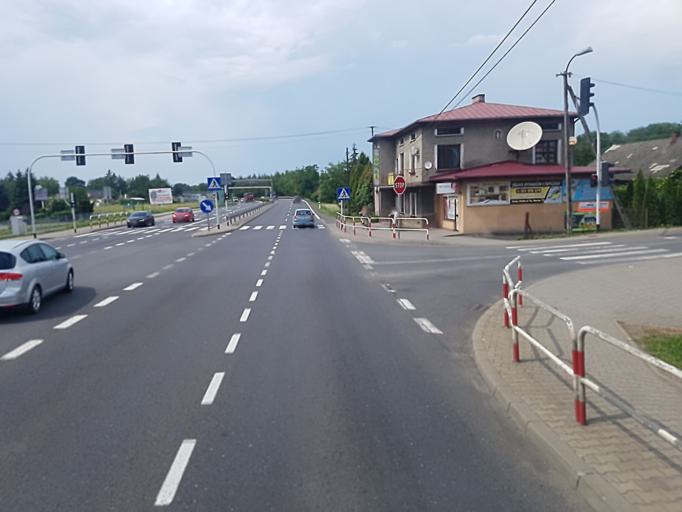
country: PL
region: Silesian Voivodeship
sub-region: Powiat cieszynski
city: Ochaby
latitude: 49.8422
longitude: 18.7690
